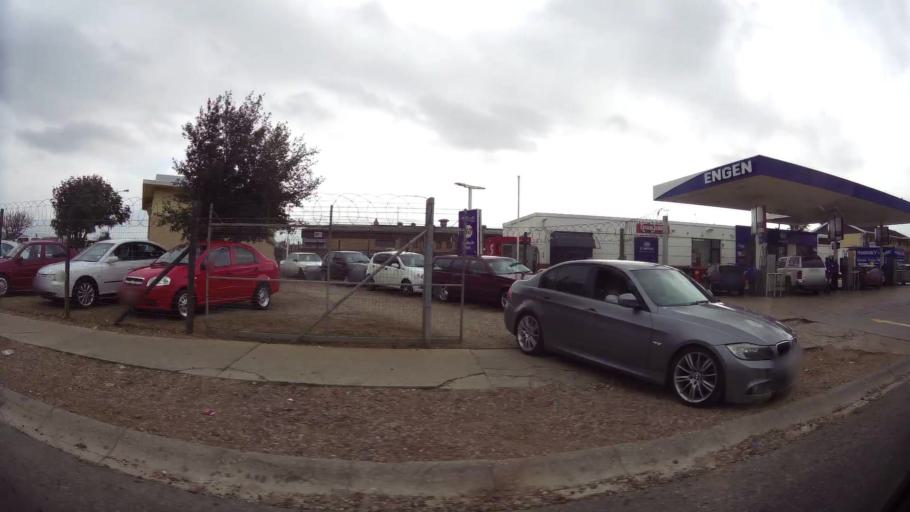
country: ZA
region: Eastern Cape
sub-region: Nelson Mandela Bay Metropolitan Municipality
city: Port Elizabeth
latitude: -33.9027
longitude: 25.5617
